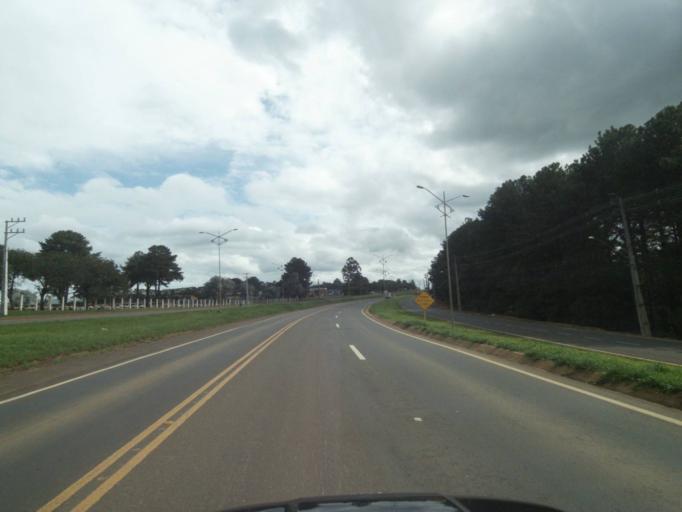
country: BR
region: Parana
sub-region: Telemaco Borba
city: Telemaco Borba
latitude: -24.3422
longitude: -50.6574
